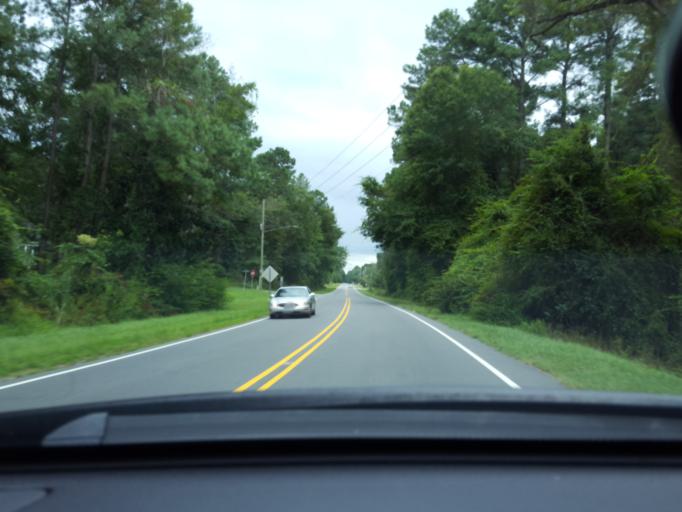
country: US
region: North Carolina
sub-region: Sampson County
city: Roseboro
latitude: 34.7829
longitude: -78.3979
